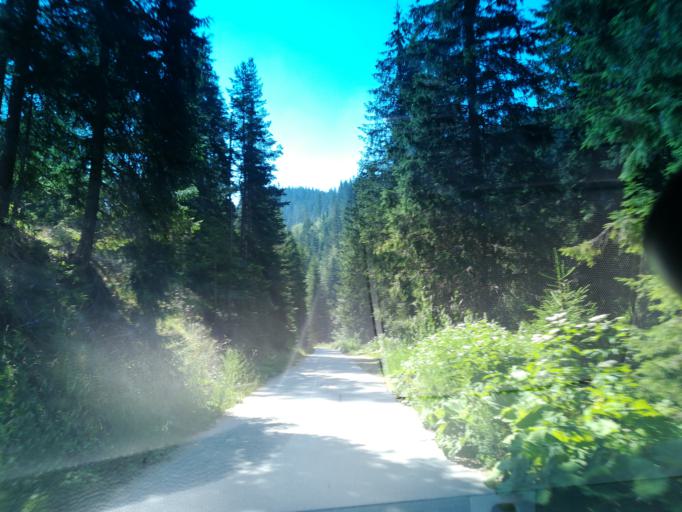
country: BG
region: Smolyan
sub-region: Obshtina Smolyan
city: Smolyan
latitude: 41.6613
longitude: 24.8049
